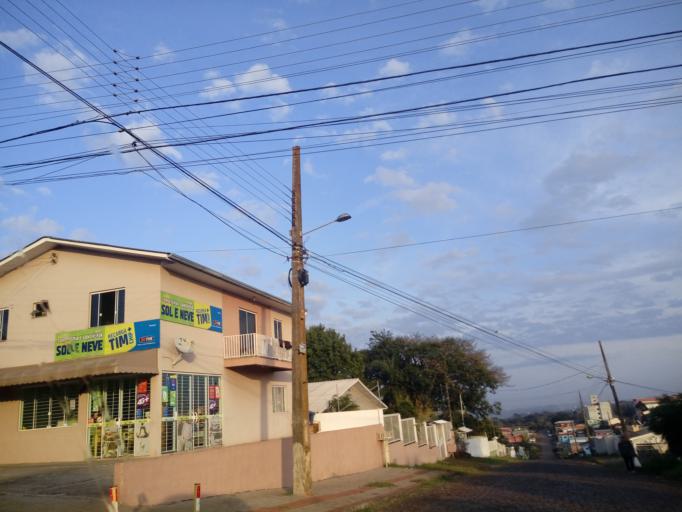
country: BR
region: Santa Catarina
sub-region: Chapeco
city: Chapeco
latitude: -27.1207
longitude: -52.6259
